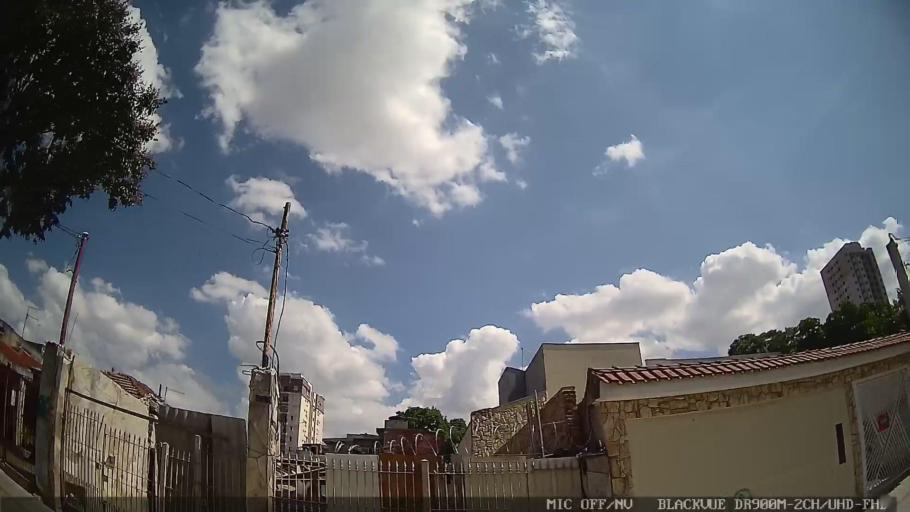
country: BR
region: Sao Paulo
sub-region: Guarulhos
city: Guarulhos
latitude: -23.4930
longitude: -46.4760
